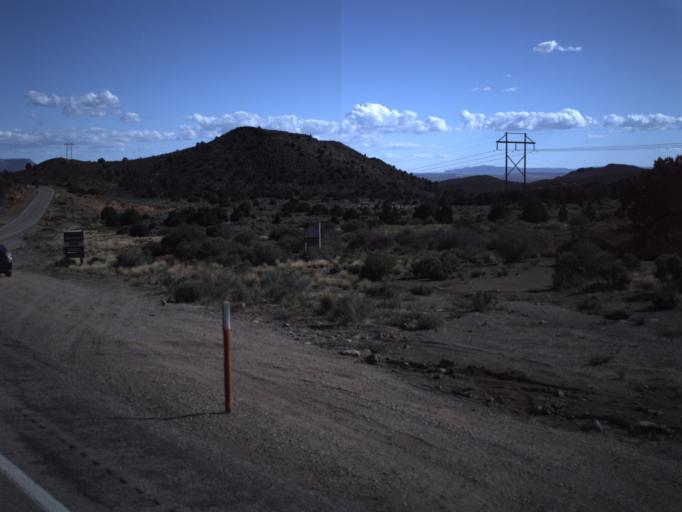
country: US
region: Utah
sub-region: Washington County
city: Toquerville
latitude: 37.2824
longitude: -113.3046
